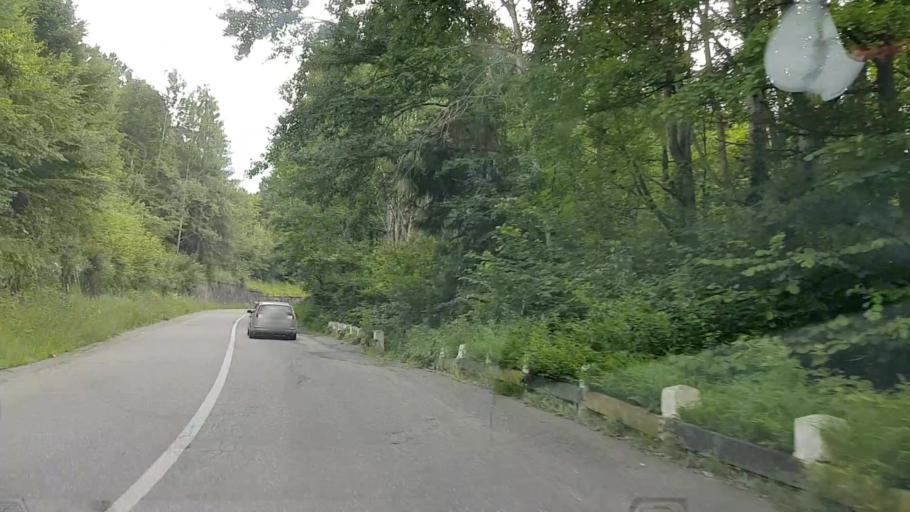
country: RO
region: Neamt
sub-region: Comuna Pangarati
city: Pangarati
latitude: 46.9457
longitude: 26.1265
